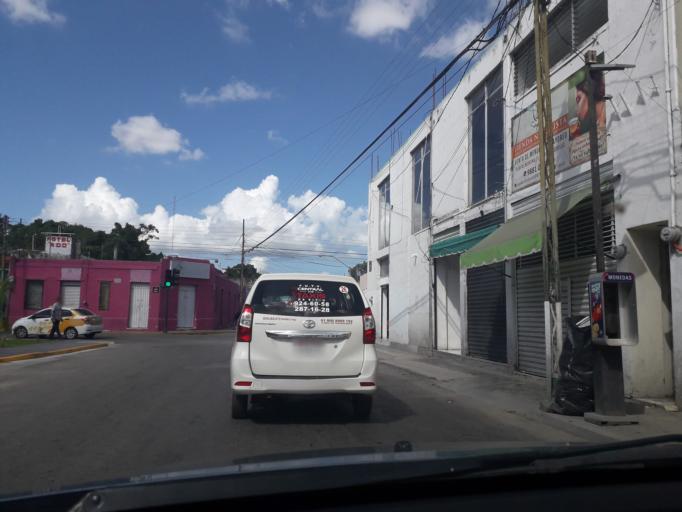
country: MX
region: Yucatan
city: Merida
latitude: 20.9627
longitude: -89.6293
